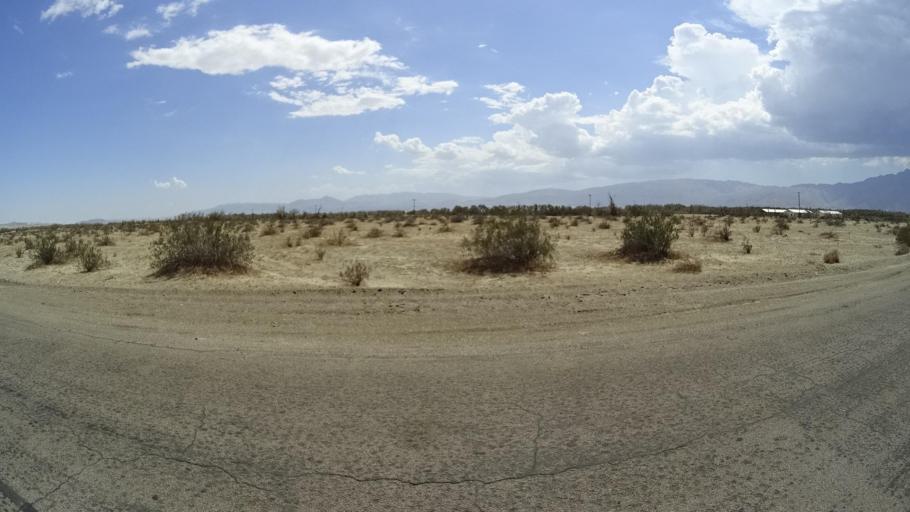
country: US
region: California
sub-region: San Diego County
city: Borrego Springs
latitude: 33.3008
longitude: -116.3363
